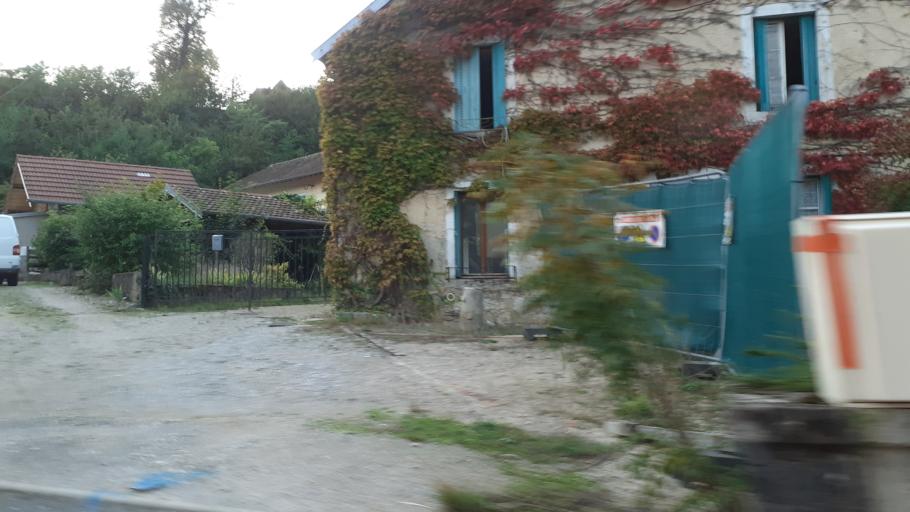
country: FR
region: Franche-Comte
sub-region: Departement du Doubs
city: Novillars
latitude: 47.2838
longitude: 6.1524
